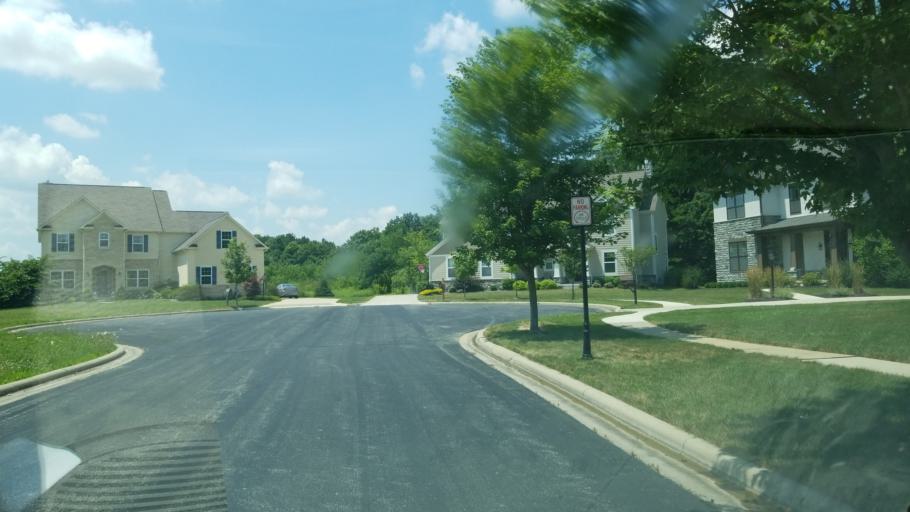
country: US
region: Ohio
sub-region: Delaware County
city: Lewis Center
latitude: 40.2537
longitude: -82.9600
